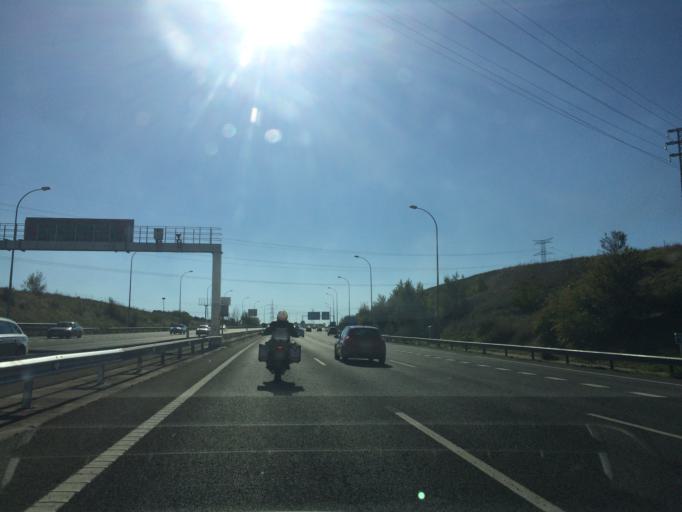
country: ES
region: Madrid
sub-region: Provincia de Madrid
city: San Sebastian de los Reyes
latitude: 40.5718
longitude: -3.5873
